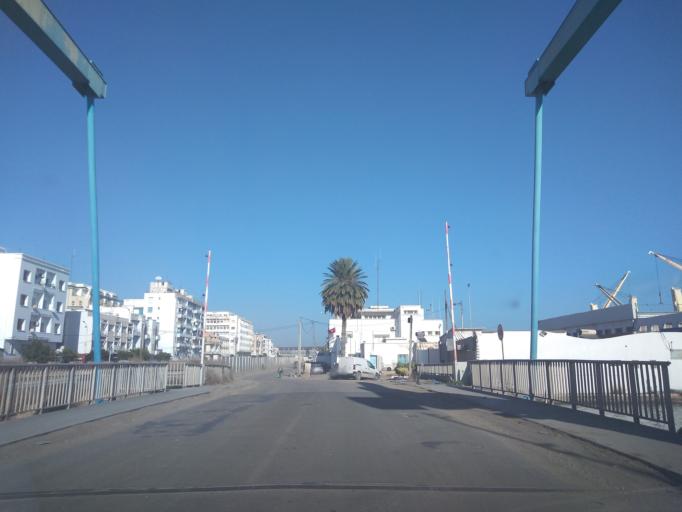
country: TN
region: Safaqis
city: Sfax
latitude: 34.7285
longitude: 10.7646
